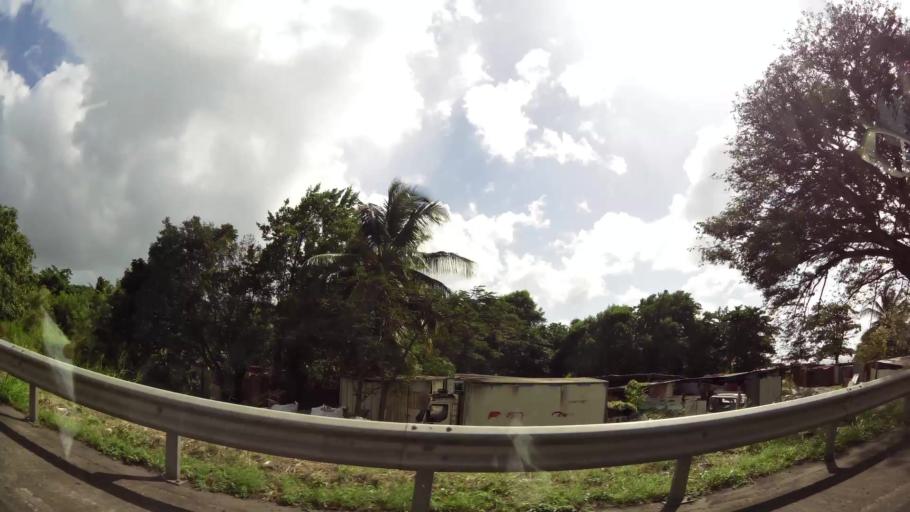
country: MQ
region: Martinique
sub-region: Martinique
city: Fort-de-France
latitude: 14.5989
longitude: -61.0517
